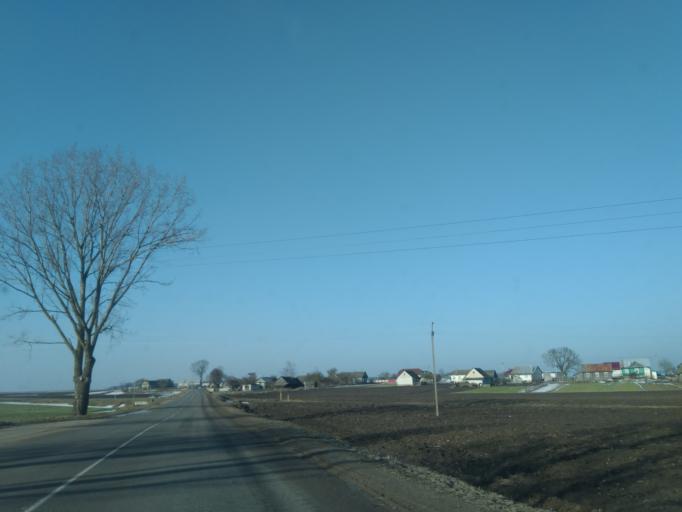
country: BY
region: Minsk
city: Snow
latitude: 53.2437
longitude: 26.3767
